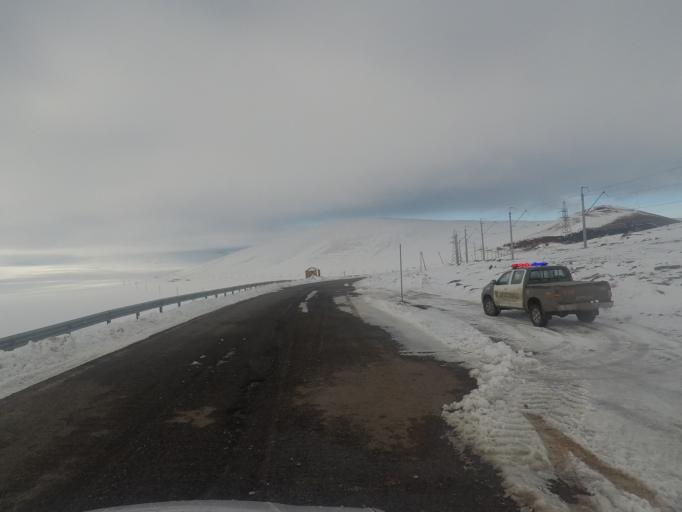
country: GE
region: Kvemo Kartli
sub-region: Tsalka
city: Tsalka
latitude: 41.4544
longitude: 43.8538
